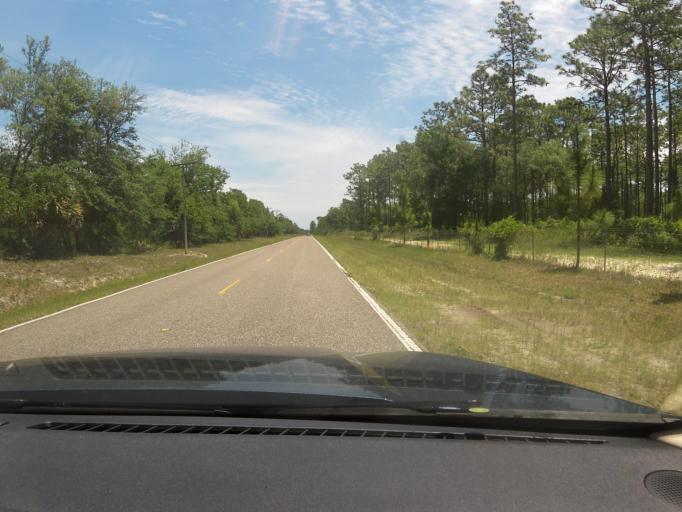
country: US
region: Florida
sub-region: Duval County
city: Atlantic Beach
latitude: 30.4587
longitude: -81.5108
